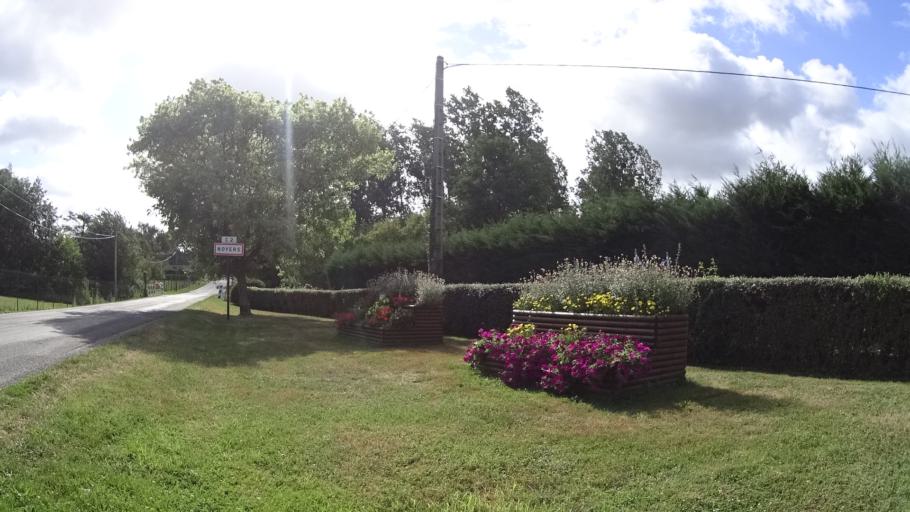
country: FR
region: Centre
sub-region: Departement du Loiret
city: Lorris
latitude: 47.9149
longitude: 2.5207
